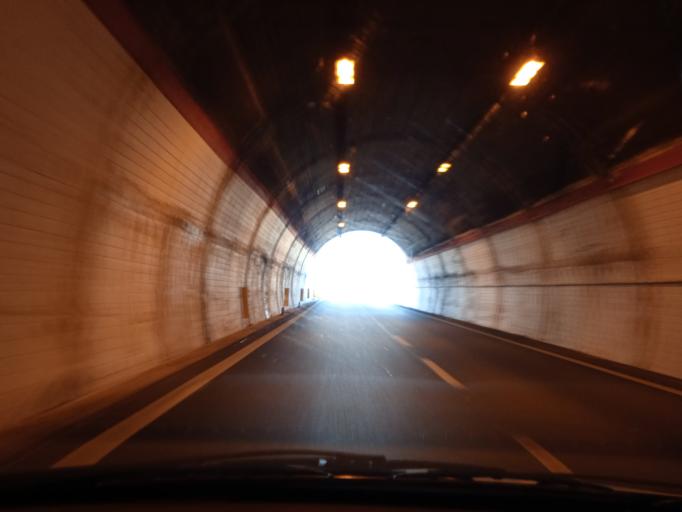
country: IT
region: Sicily
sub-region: Palermo
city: Cinisi
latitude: 38.1792
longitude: 13.1260
